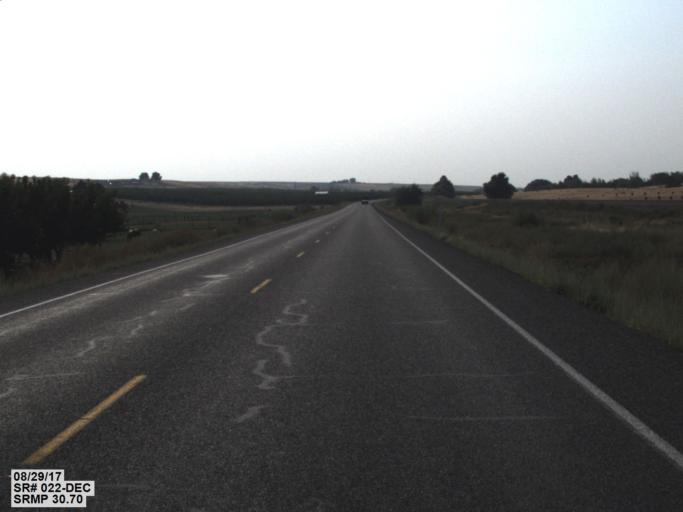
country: US
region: Washington
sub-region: Benton County
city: Prosser
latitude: 46.1867
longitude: -119.8470
